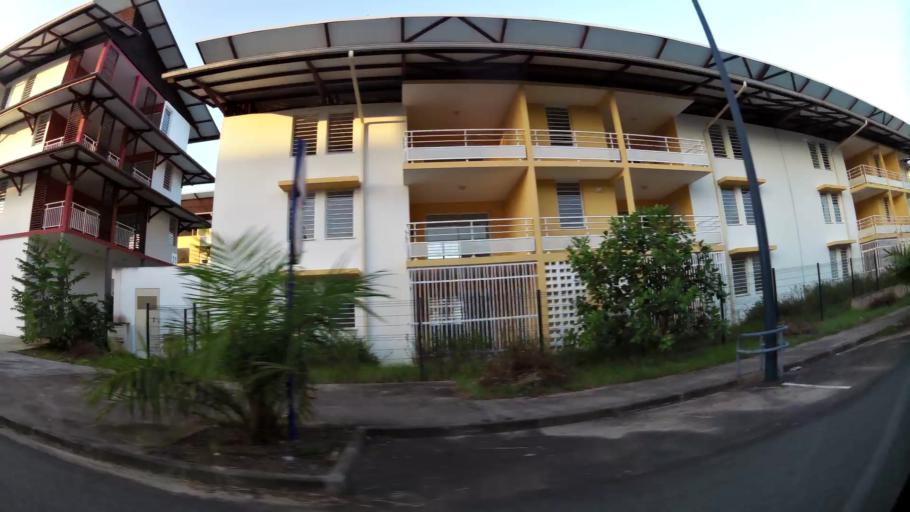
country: GF
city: Macouria
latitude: 4.9312
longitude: -52.4079
